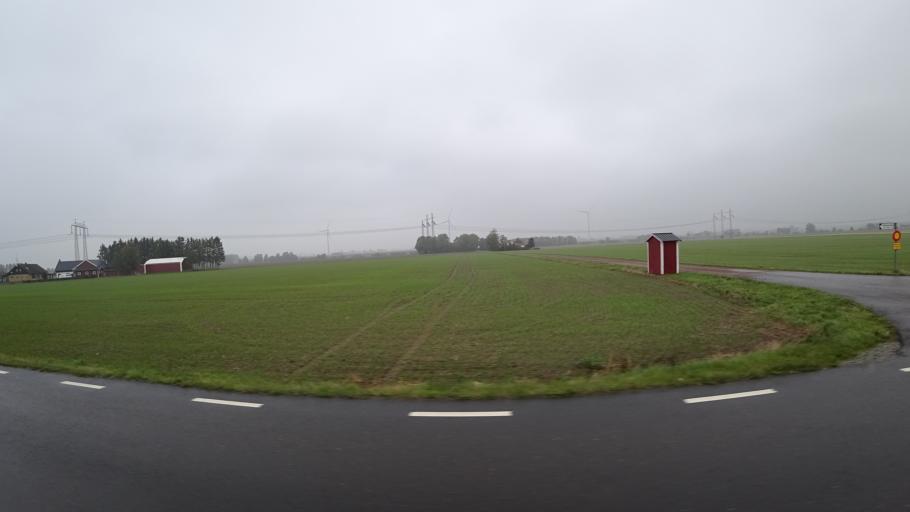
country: SE
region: Skane
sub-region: Kavlinge Kommun
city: Kaevlinge
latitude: 55.8172
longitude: 13.1296
